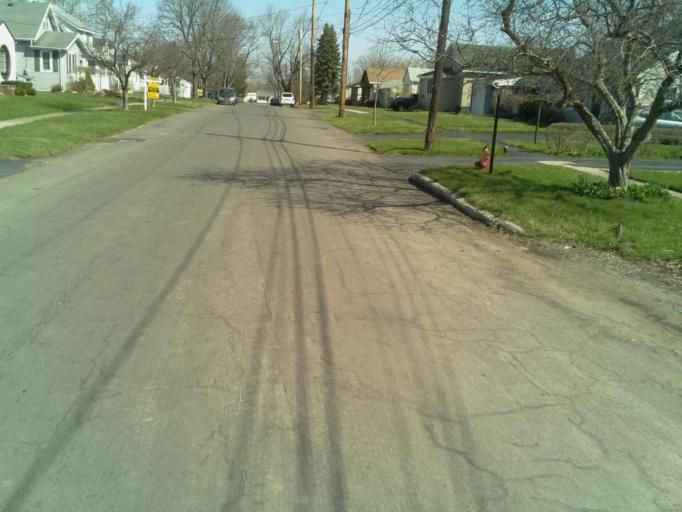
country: US
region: New York
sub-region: Onondaga County
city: Lyncourt
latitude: 43.0721
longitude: -76.1030
